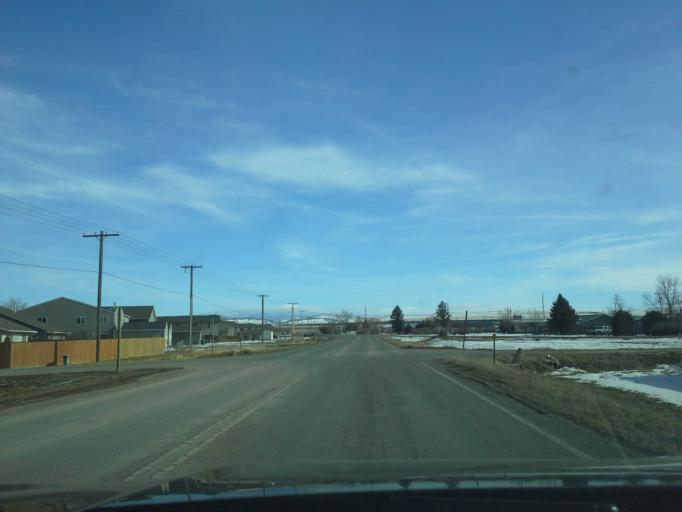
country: US
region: Montana
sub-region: Lewis and Clark County
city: East Helena
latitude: 46.5883
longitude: -111.8996
